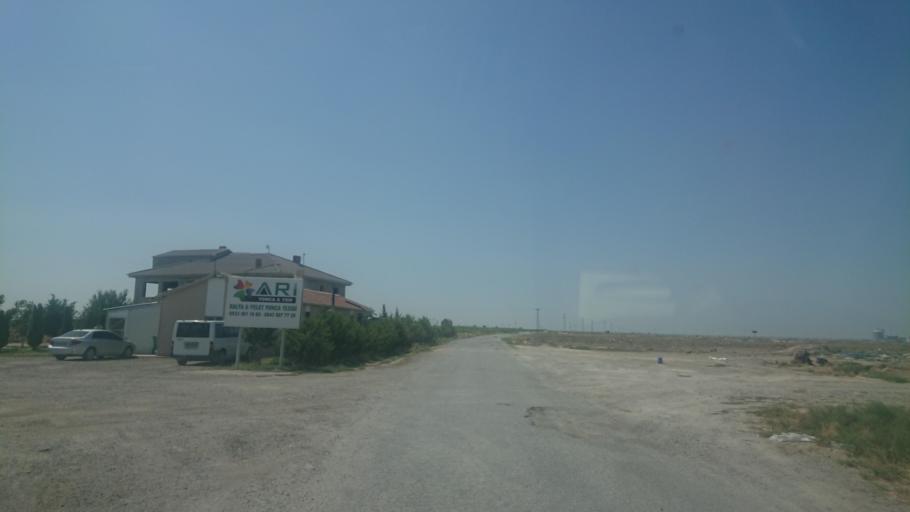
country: TR
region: Aksaray
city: Sultanhani
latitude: 38.2827
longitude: 33.7084
